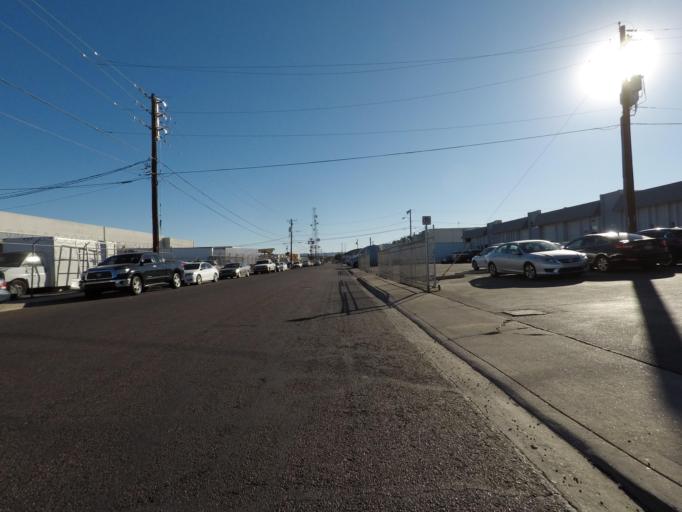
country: US
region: Arizona
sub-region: Maricopa County
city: Phoenix
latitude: 33.4715
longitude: -112.1086
